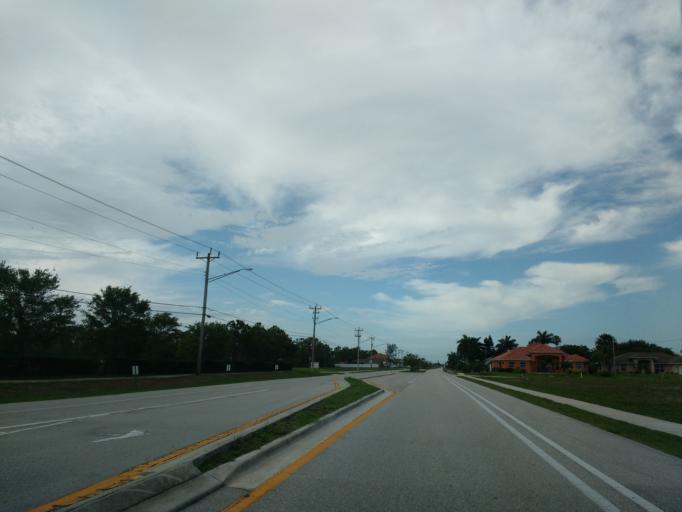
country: US
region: Florida
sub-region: Lee County
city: Cape Coral
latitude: 26.5872
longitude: -82.0241
